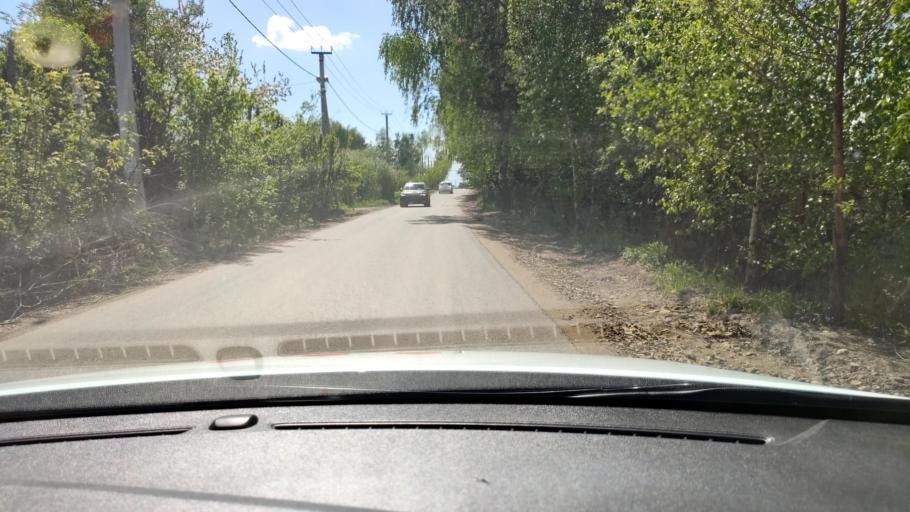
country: RU
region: Tatarstan
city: Vysokaya Gora
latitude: 55.8148
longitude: 49.2797
